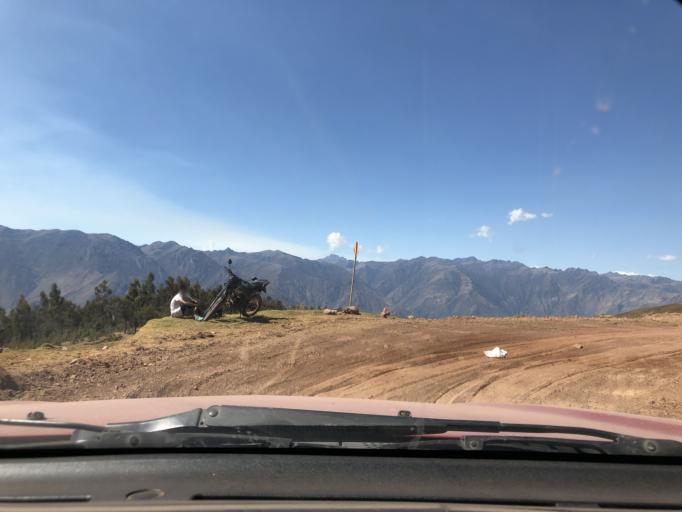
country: PE
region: Ayacucho
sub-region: Provincia de La Mar
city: Chilcas
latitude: -13.1811
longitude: -73.8409
